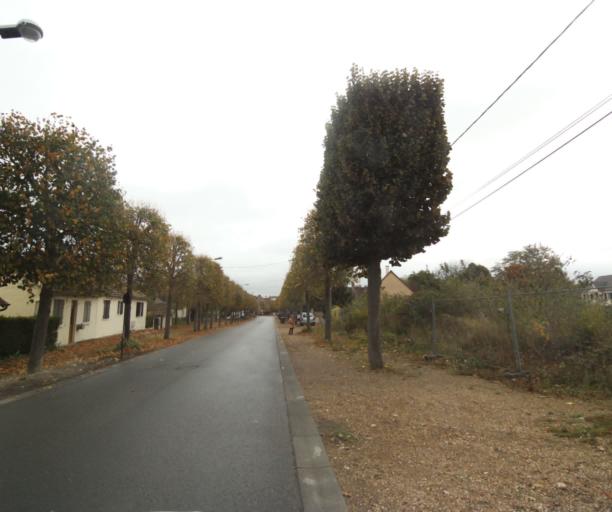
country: FR
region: Centre
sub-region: Departement d'Eure-et-Loir
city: Dreux
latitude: 48.7388
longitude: 1.3803
